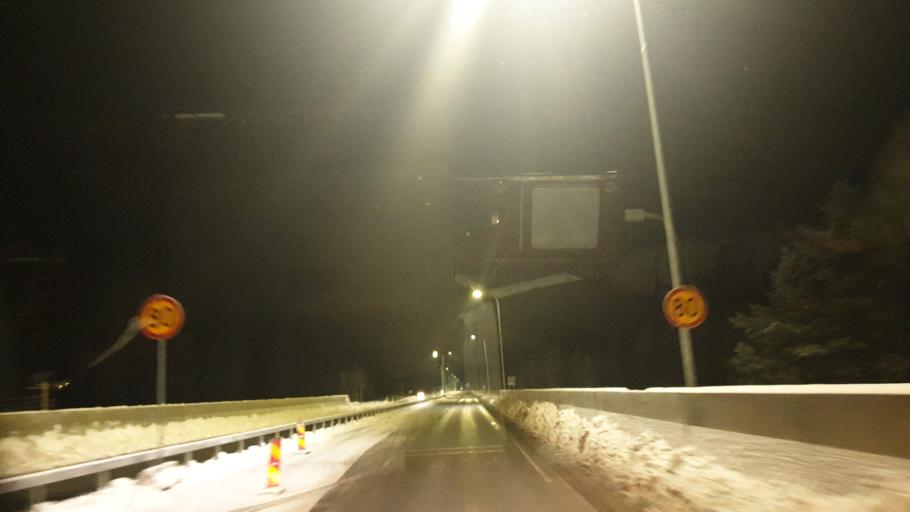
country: FI
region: Northern Ostrobothnia
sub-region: Oulu
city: Haukipudas
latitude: 65.1879
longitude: 25.4273
